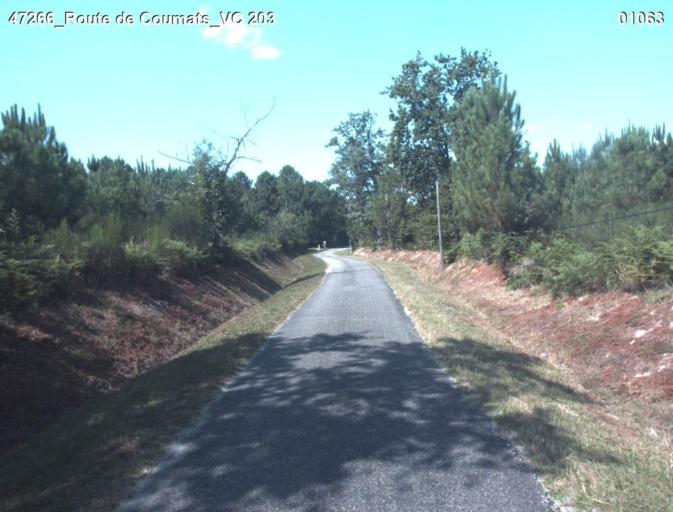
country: FR
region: Aquitaine
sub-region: Departement des Landes
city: Gabarret
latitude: 44.0085
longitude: 0.0919
